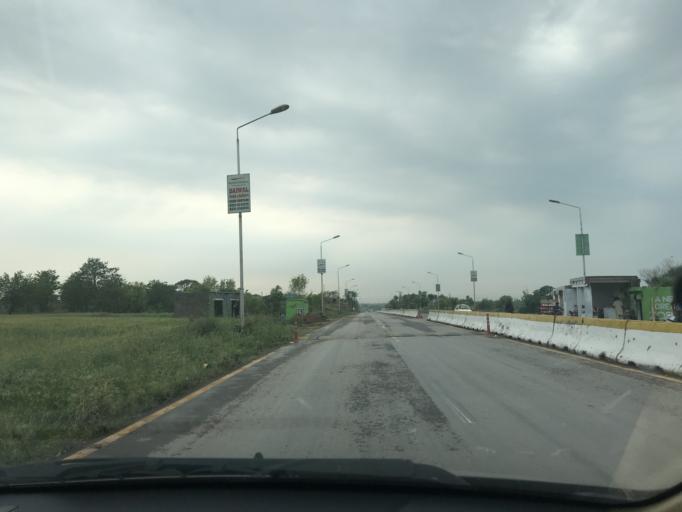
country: PK
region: Islamabad
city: Islamabad
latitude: 33.7015
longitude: 73.1879
